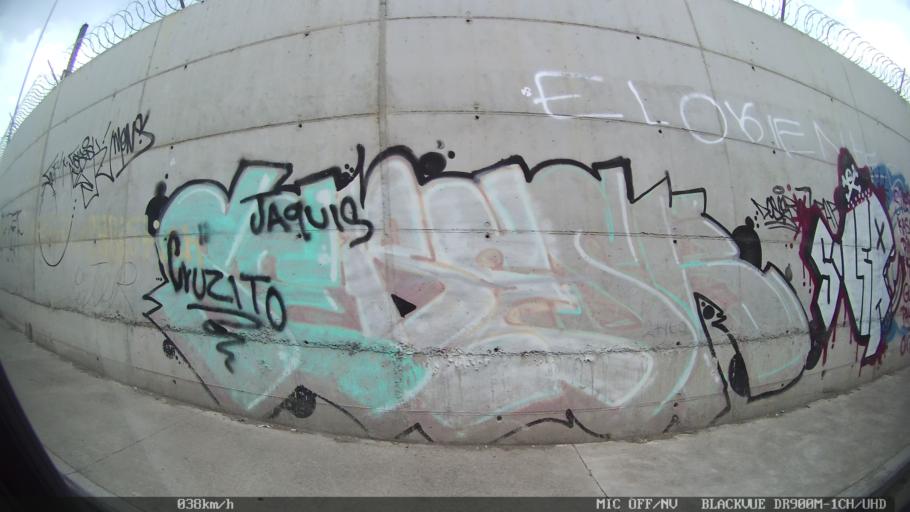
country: MX
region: Jalisco
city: Tlaquepaque
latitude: 20.6186
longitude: -103.2770
